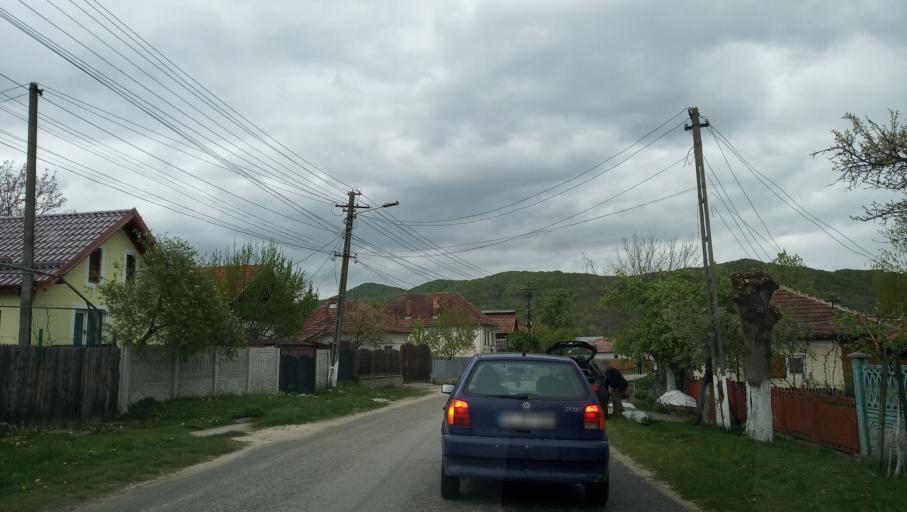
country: RO
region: Valcea
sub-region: Municipiul Ramnicu Valcea
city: Goranu
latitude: 45.1504
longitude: 24.3944
